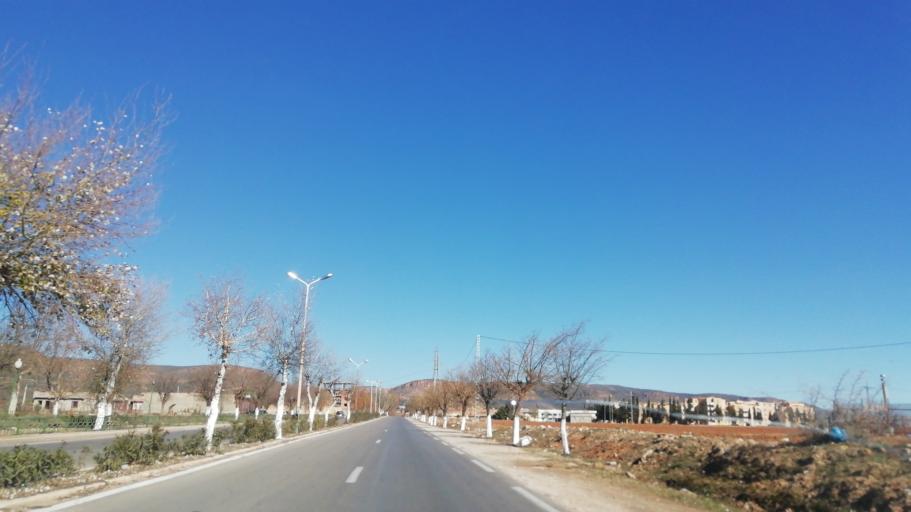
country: DZ
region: Tlemcen
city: Sebdou
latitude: 34.6598
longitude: -1.3235
